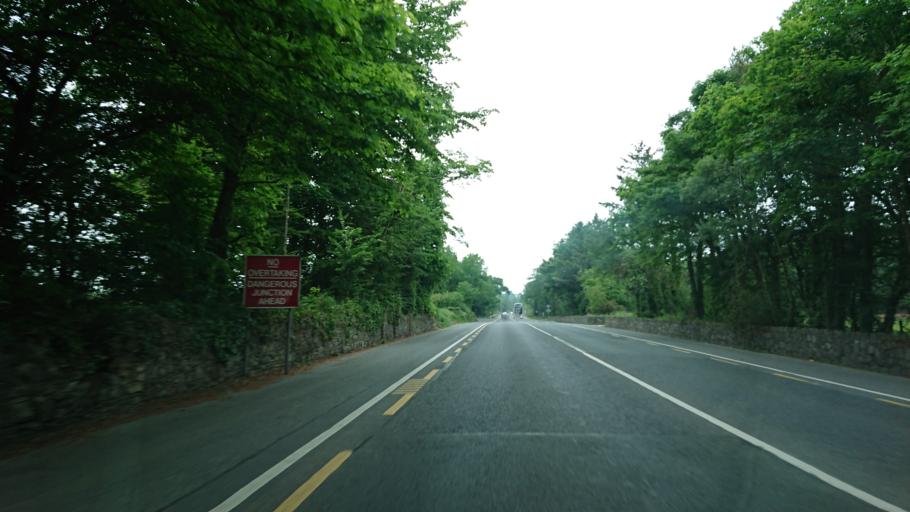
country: IE
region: Munster
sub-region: Waterford
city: Waterford
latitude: 52.2179
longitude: -7.1265
